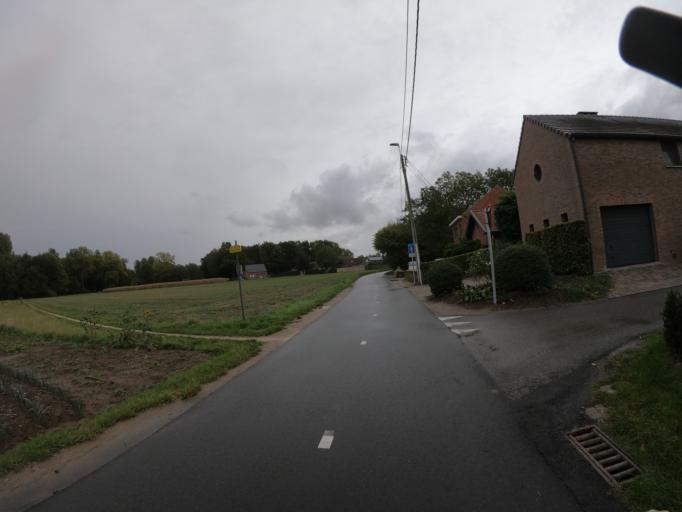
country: BE
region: Flanders
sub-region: Provincie Vlaams-Brabant
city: Rotselaar
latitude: 50.9487
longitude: 4.7311
